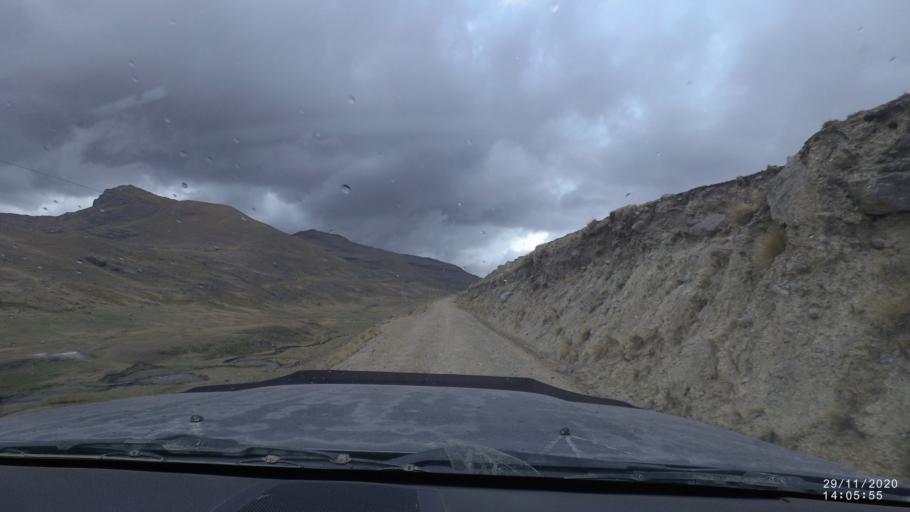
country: BO
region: Cochabamba
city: Sipe Sipe
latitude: -17.2099
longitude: -66.3769
